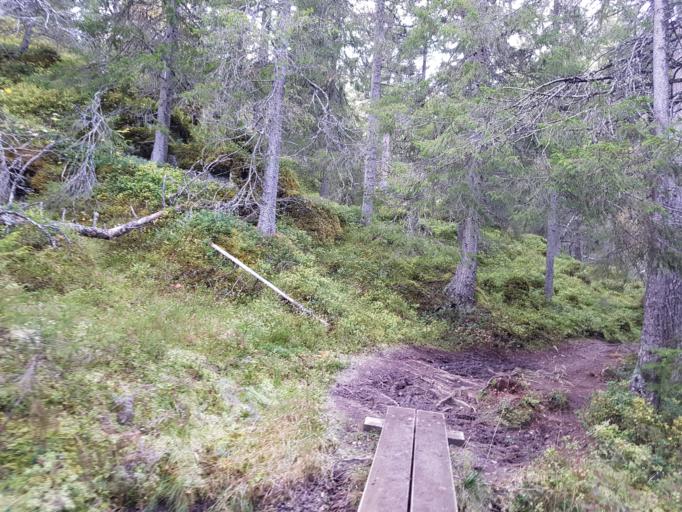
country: NO
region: Sor-Trondelag
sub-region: Trondheim
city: Trondheim
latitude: 63.4480
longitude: 10.2701
